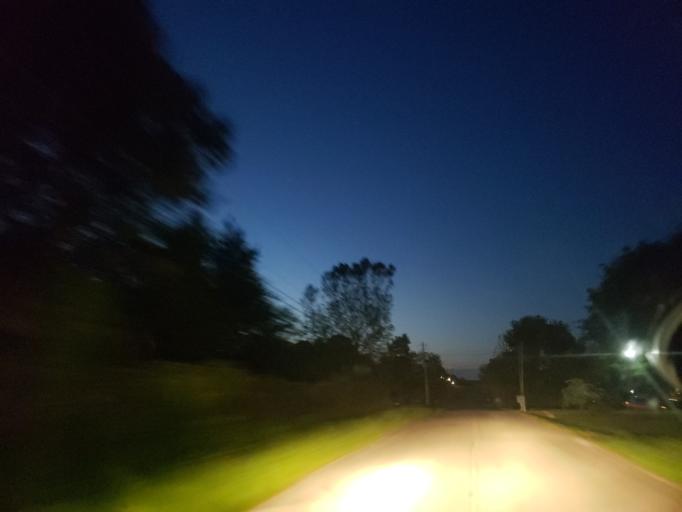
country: US
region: Alabama
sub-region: Madison County
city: Hazel Green
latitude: 34.9746
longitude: -86.6681
